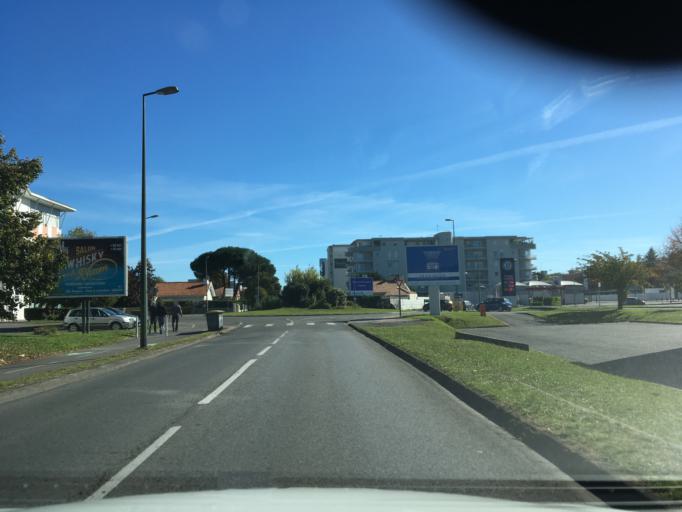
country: FR
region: Aquitaine
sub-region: Departement des Pyrenees-Atlantiques
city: Pau
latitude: 43.3182
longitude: -0.3570
